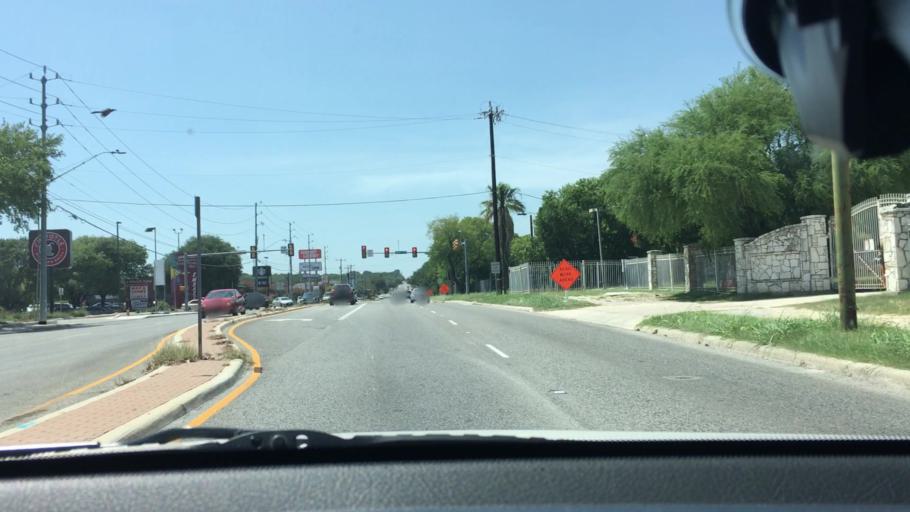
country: US
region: Texas
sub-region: Bexar County
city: Hollywood Park
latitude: 29.5662
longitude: -98.4840
